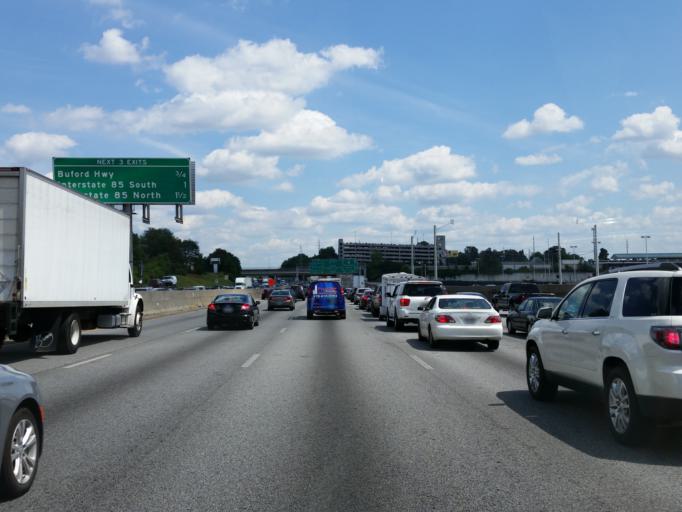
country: US
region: Georgia
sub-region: DeKalb County
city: Doraville
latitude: 33.9086
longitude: -84.2820
